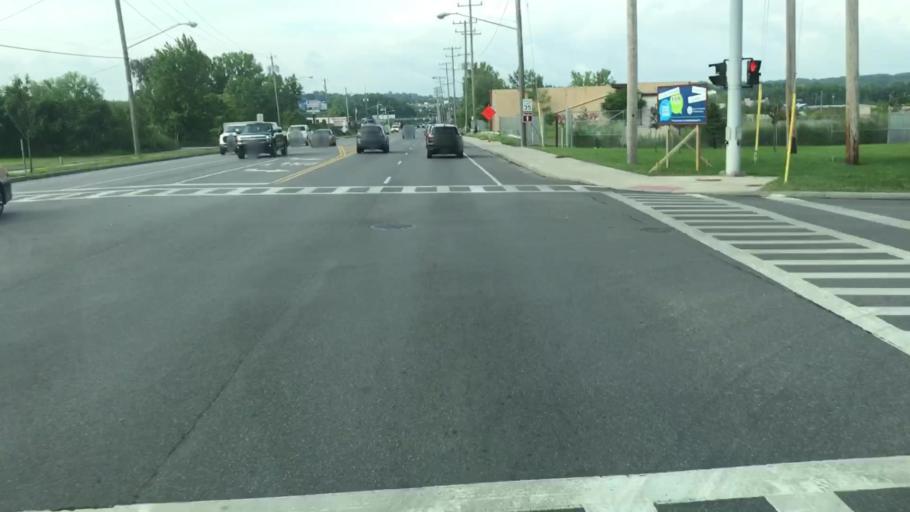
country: US
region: New York
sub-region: Onondaga County
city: Galeville
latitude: 43.0623
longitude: -76.1767
